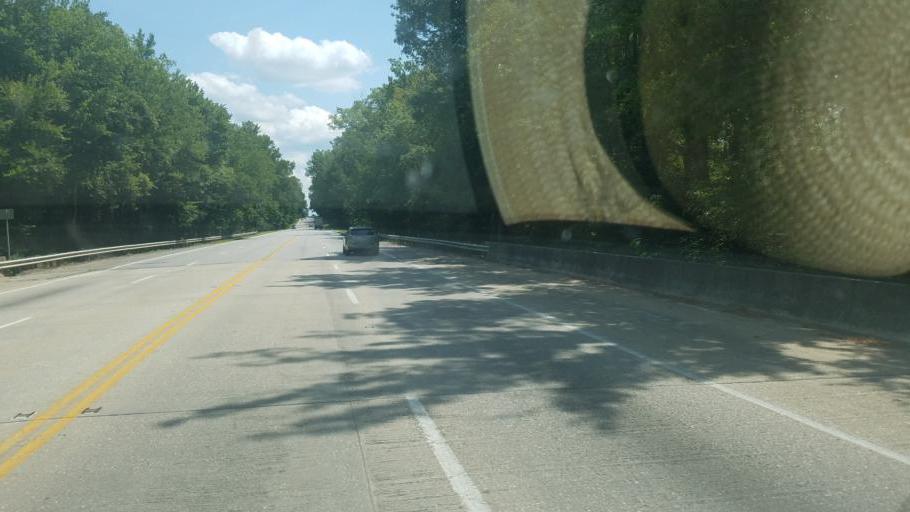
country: US
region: Virginia
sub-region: Sussex County
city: Waverly
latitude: 37.0878
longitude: -77.1667
